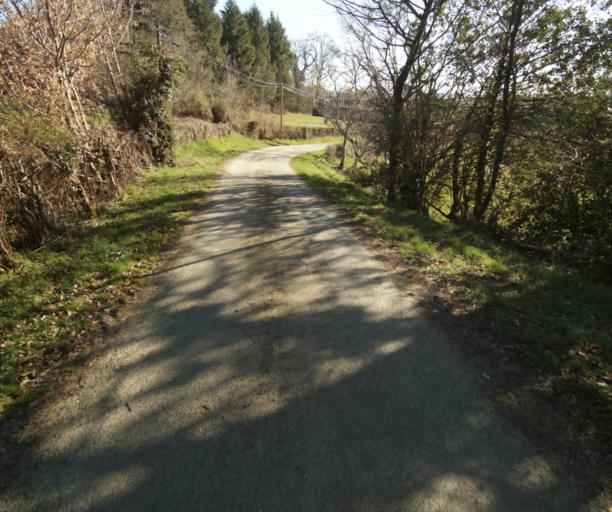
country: FR
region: Limousin
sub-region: Departement de la Correze
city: Seilhac
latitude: 45.3814
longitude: 1.7645
